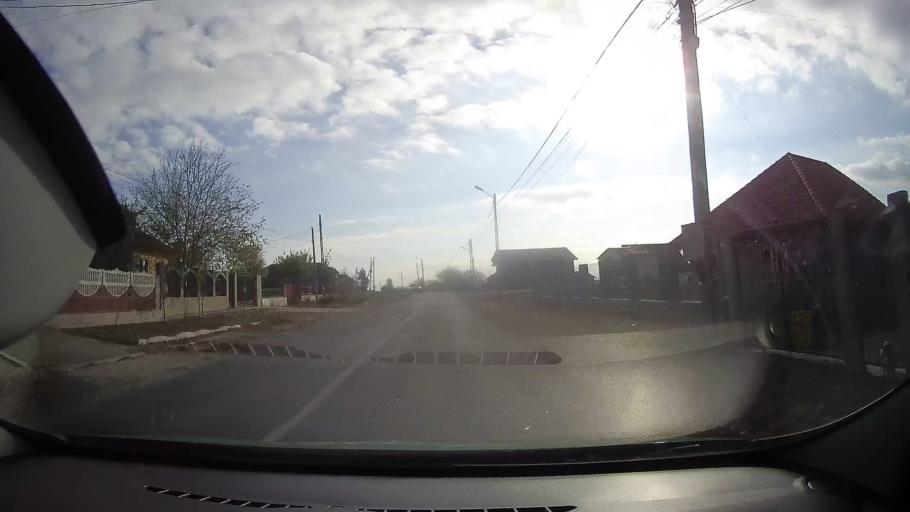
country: RO
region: Constanta
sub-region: Comuna Corbu
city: Corbu
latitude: 44.4064
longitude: 28.6617
